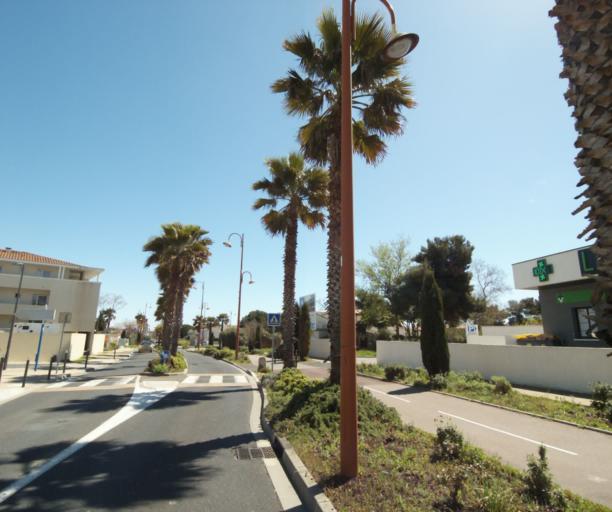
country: FR
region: Languedoc-Roussillon
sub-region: Departement de l'Herault
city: Perols
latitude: 43.5613
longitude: 3.9517
